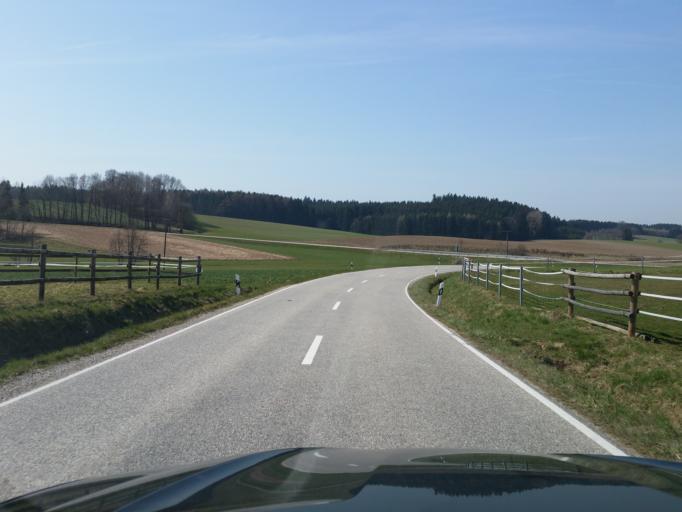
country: DE
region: Bavaria
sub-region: Lower Bavaria
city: Vilsheim
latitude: 48.4428
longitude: 12.1001
